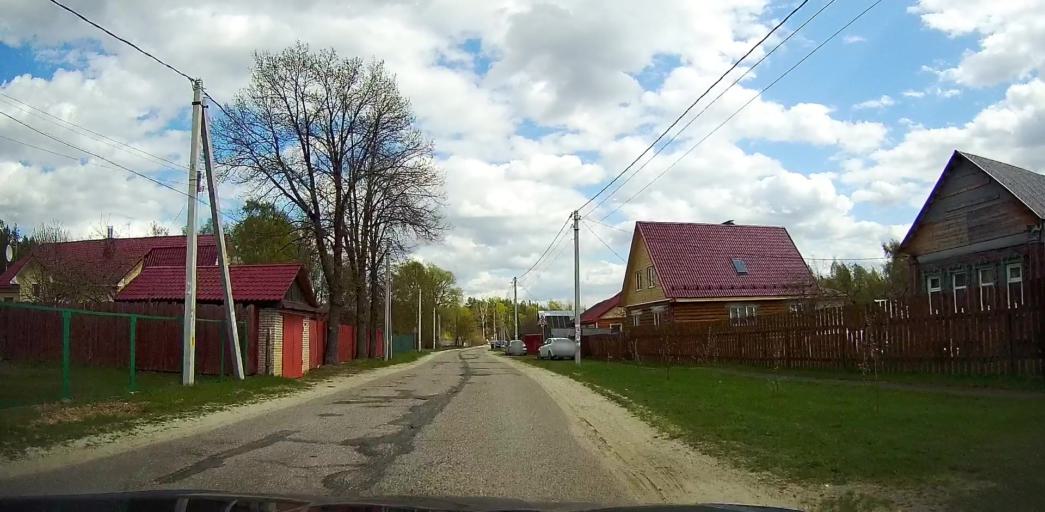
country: RU
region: Moskovskaya
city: Davydovo
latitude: 55.6473
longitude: 38.7644
